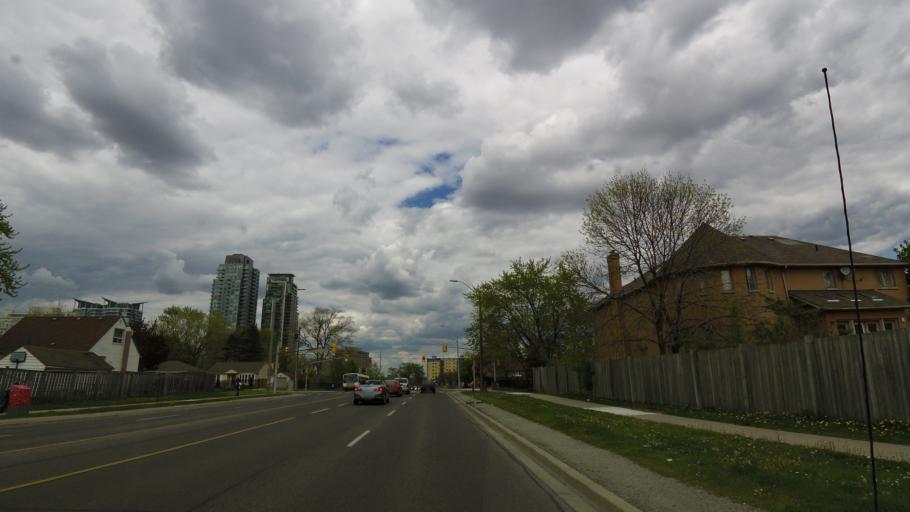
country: CA
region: Ontario
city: Mississauga
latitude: 43.5853
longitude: -79.6334
